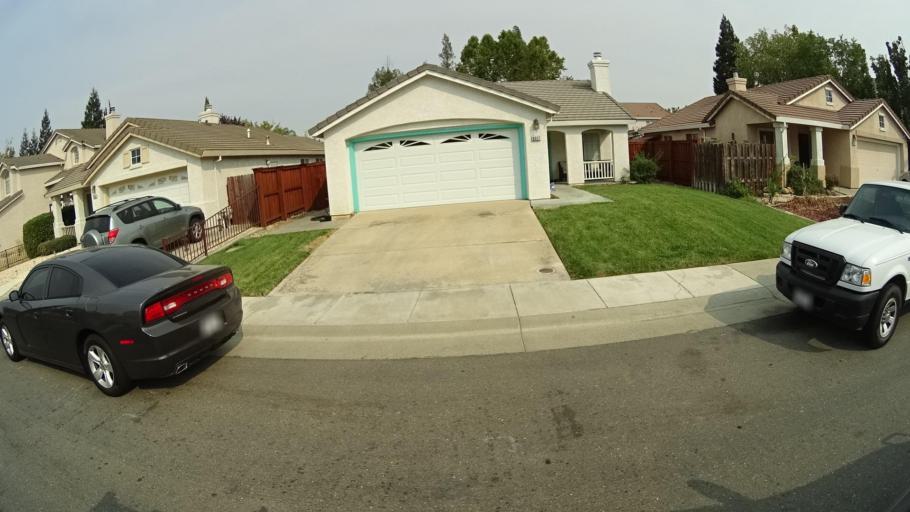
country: US
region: California
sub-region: Sacramento County
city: Laguna
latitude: 38.4109
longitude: -121.4067
